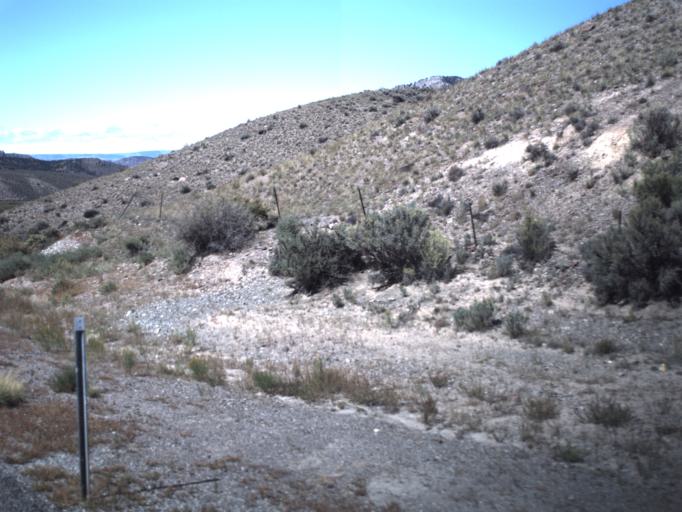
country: US
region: Utah
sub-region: Piute County
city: Junction
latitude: 38.1684
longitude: -112.0536
